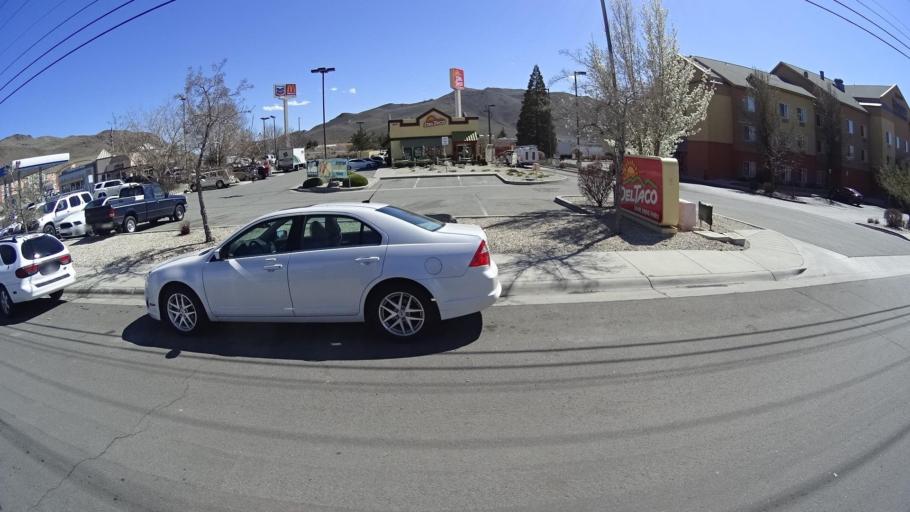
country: US
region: Nevada
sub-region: Washoe County
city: Sparks
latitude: 39.5279
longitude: -119.7022
